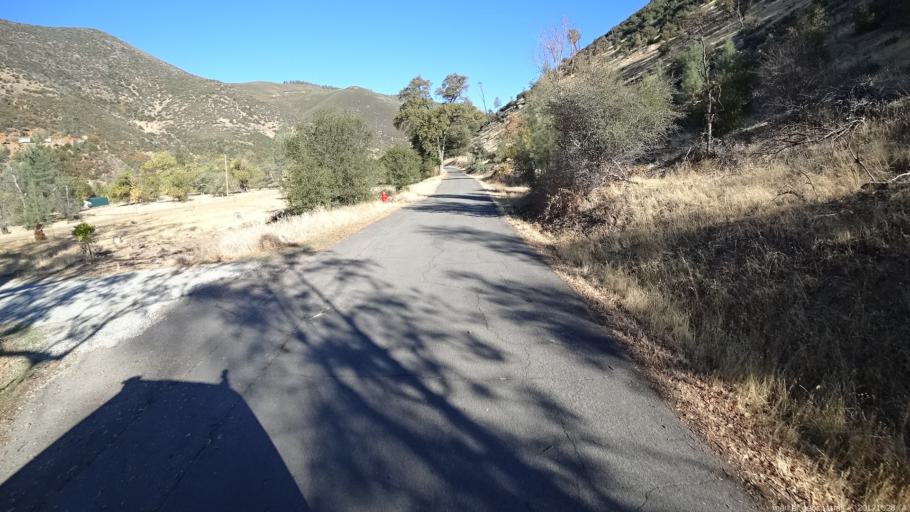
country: US
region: California
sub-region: Trinity County
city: Lewiston
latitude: 40.7096
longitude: -122.6348
